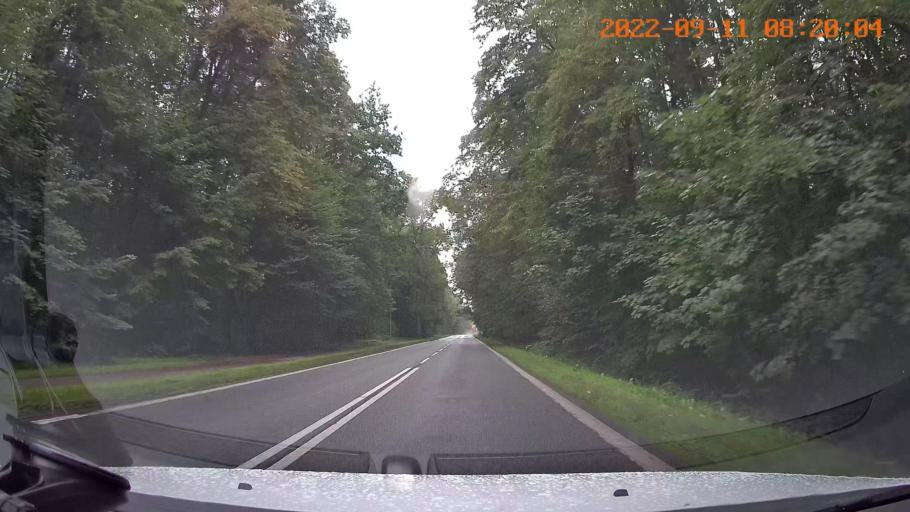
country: PL
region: Silesian Voivodeship
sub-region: Tychy
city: Tychy
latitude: 50.1561
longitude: 19.0084
